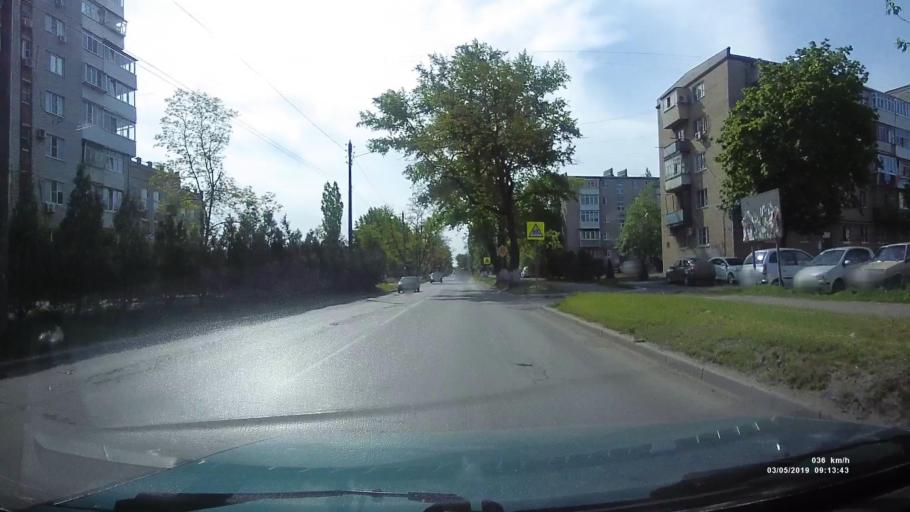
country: RU
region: Rostov
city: Azov
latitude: 47.0994
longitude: 39.4245
